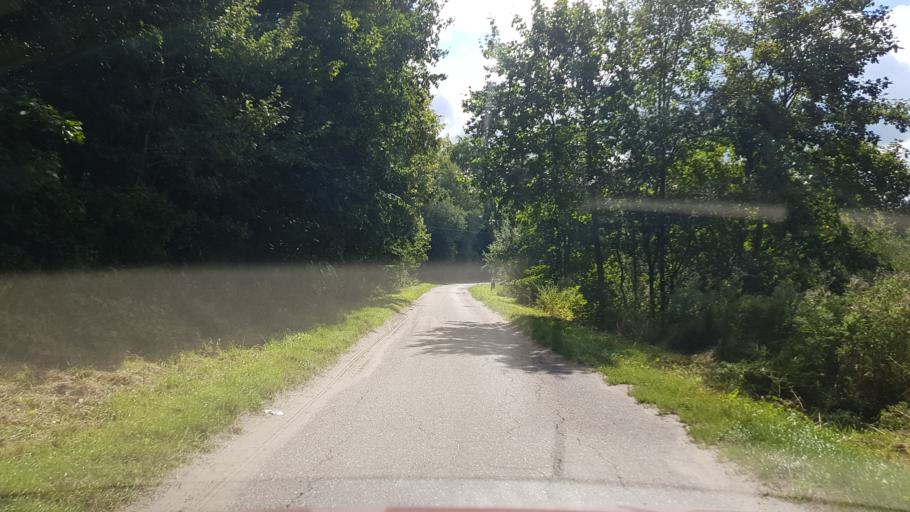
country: PL
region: West Pomeranian Voivodeship
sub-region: Powiat bialogardzki
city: Tychowo
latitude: 53.9911
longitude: 16.3028
